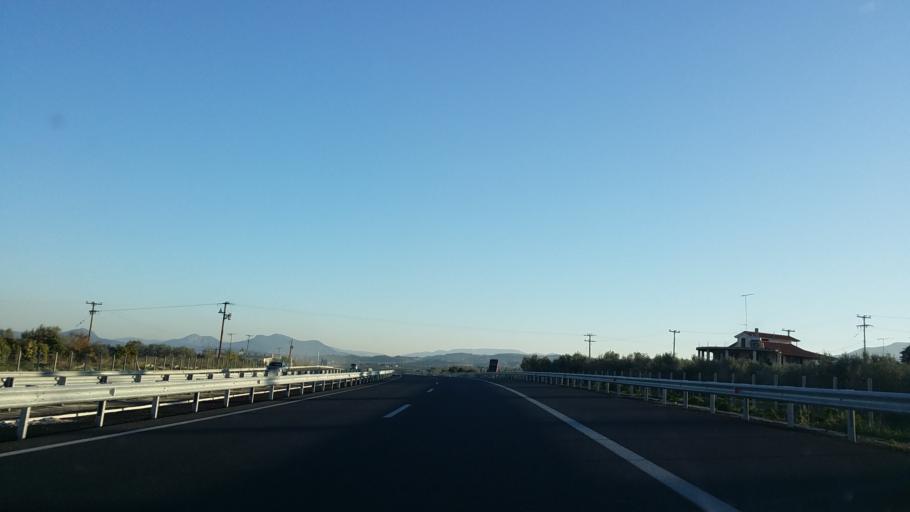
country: GR
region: Peloponnese
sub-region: Nomos Korinthias
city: Velo
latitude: 37.9596
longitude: 22.7491
